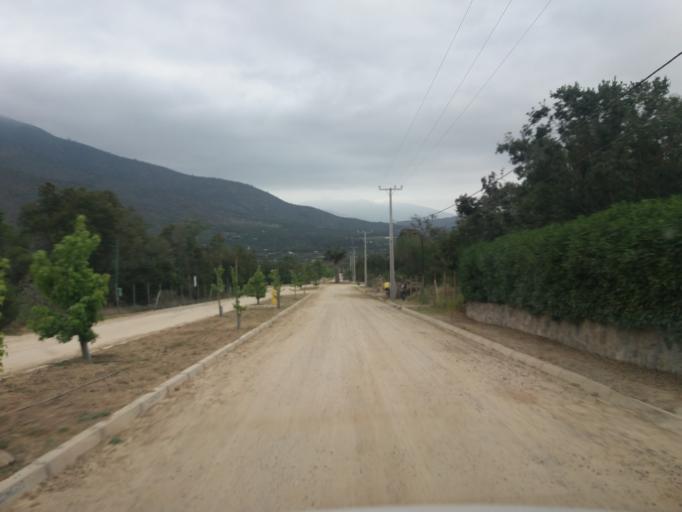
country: CL
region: Valparaiso
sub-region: Provincia de Marga Marga
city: Limache
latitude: -33.0256
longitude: -71.1307
